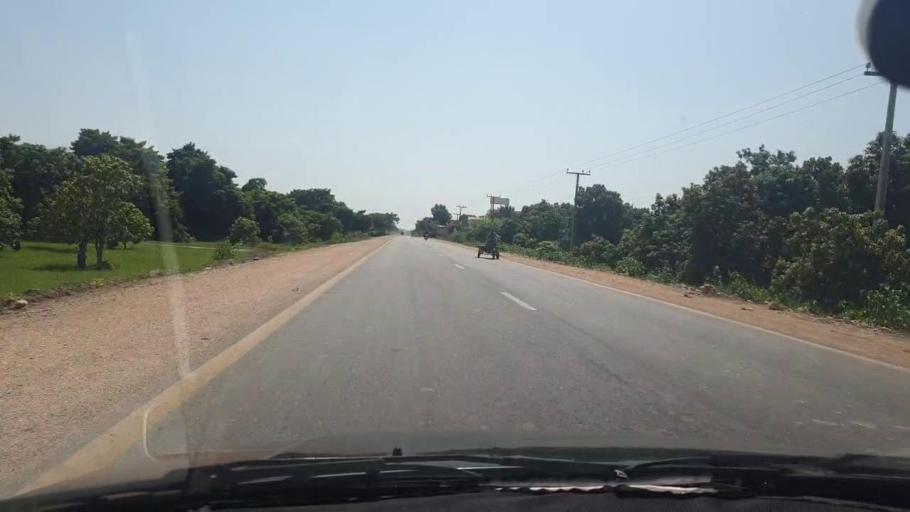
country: PK
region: Sindh
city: Chambar
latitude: 25.3230
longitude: 68.8014
